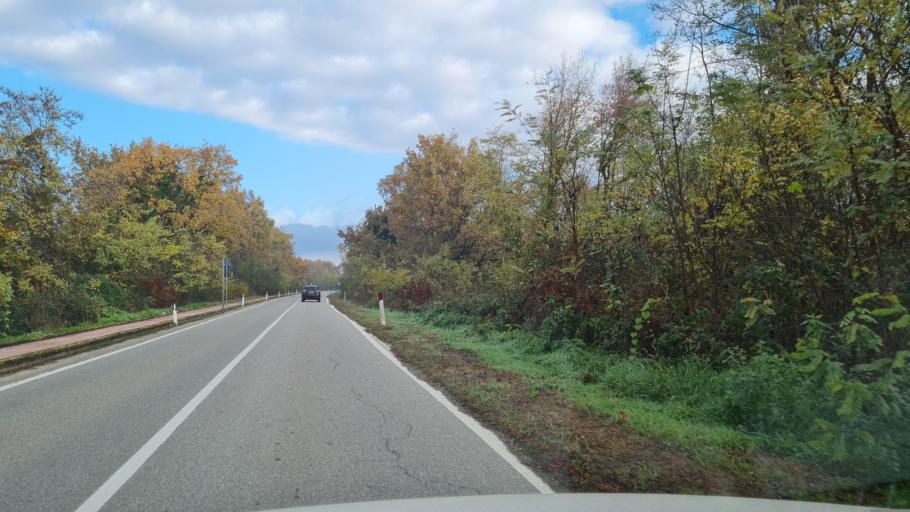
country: IT
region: Piedmont
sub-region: Provincia di Biella
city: Castelletto Cervo
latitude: 45.5226
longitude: 8.2233
